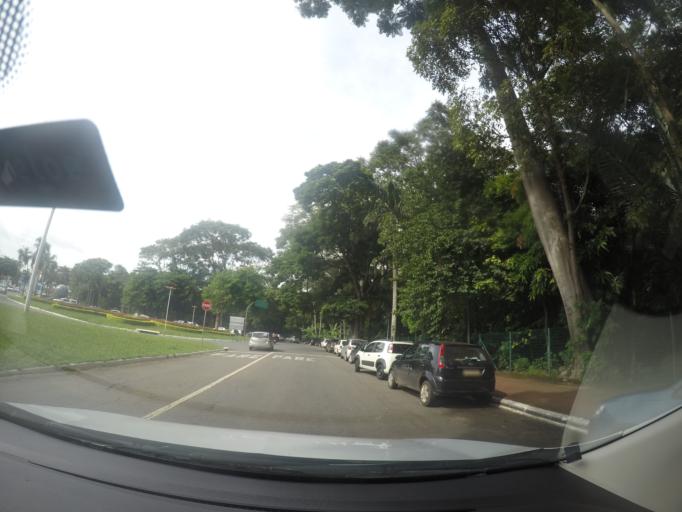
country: BR
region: Goias
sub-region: Goiania
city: Goiania
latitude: -16.6814
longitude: -49.2604
